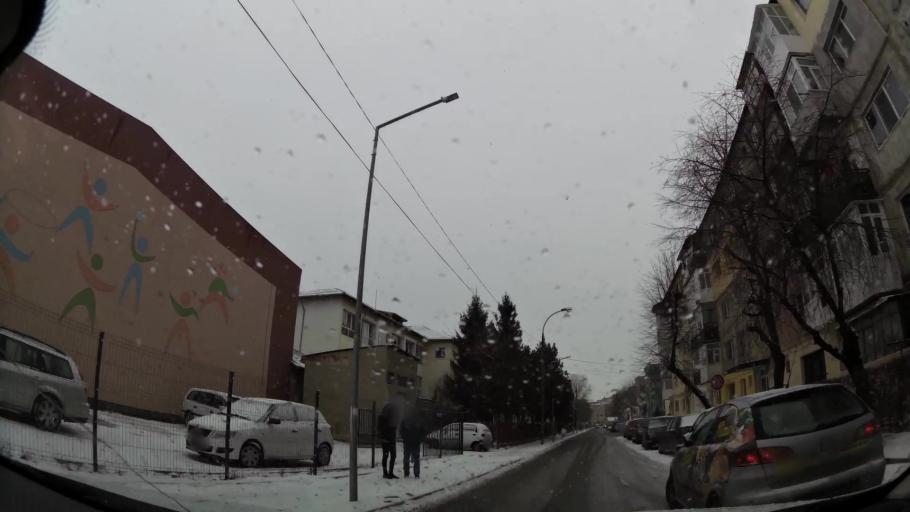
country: RO
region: Dambovita
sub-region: Municipiul Targoviste
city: Targoviste
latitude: 44.9245
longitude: 25.4450
